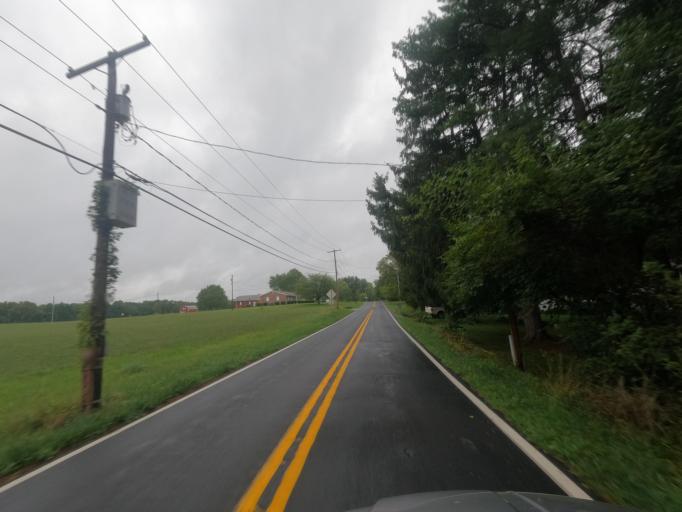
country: US
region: West Virginia
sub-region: Berkeley County
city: Martinsburg
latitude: 39.6186
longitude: -77.9934
